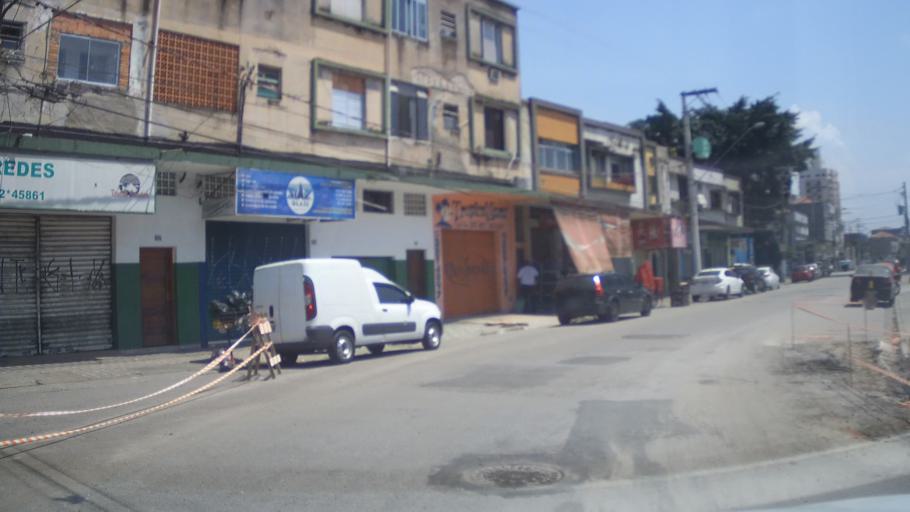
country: BR
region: Sao Paulo
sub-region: Guaruja
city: Guaruja
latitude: -23.9857
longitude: -46.2962
